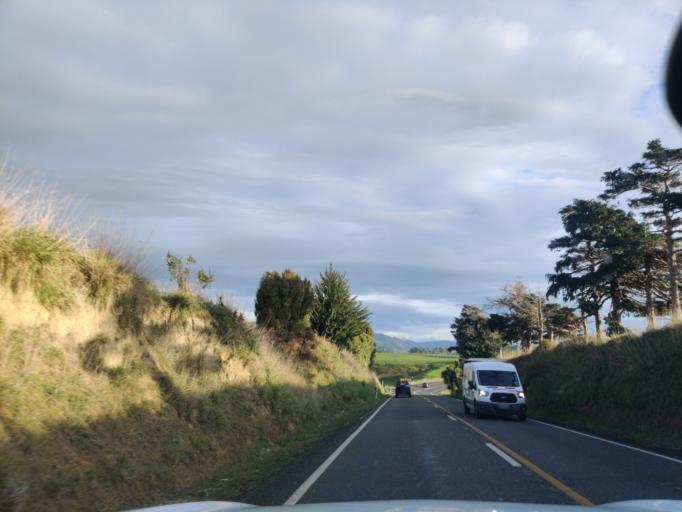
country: NZ
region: Manawatu-Wanganui
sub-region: Horowhenua District
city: Foxton
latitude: -40.5063
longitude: 175.4855
